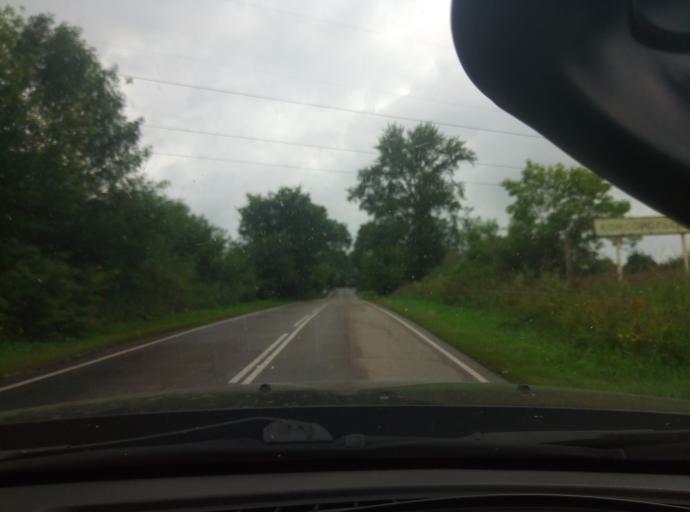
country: RU
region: Tula
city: Lomintsevskiy
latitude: 53.9577
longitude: 37.6722
